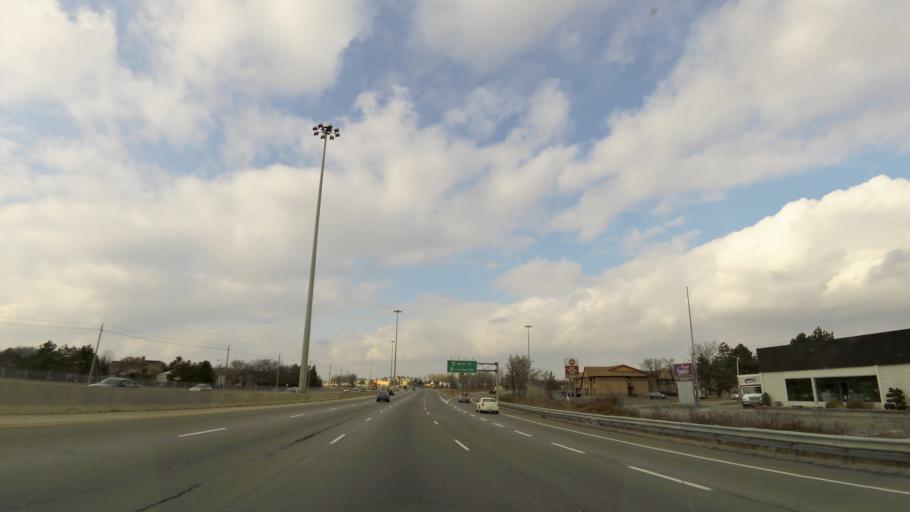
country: CA
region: Ontario
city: Kitchener
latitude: 43.4274
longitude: -80.4364
